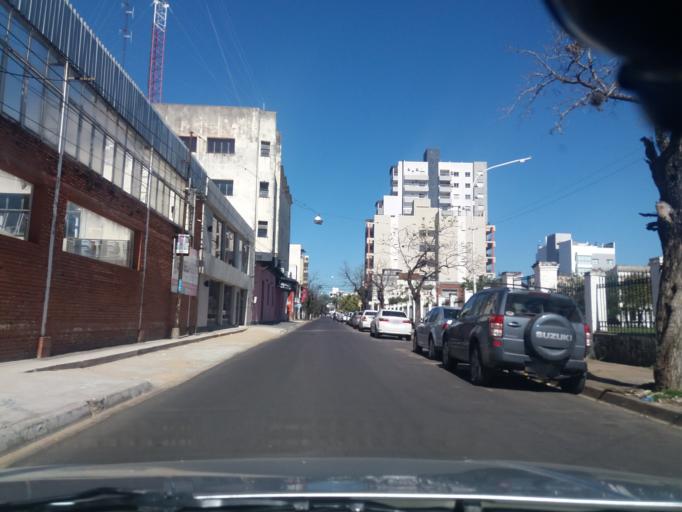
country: AR
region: Corrientes
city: Corrientes
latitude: -27.4723
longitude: -58.8395
